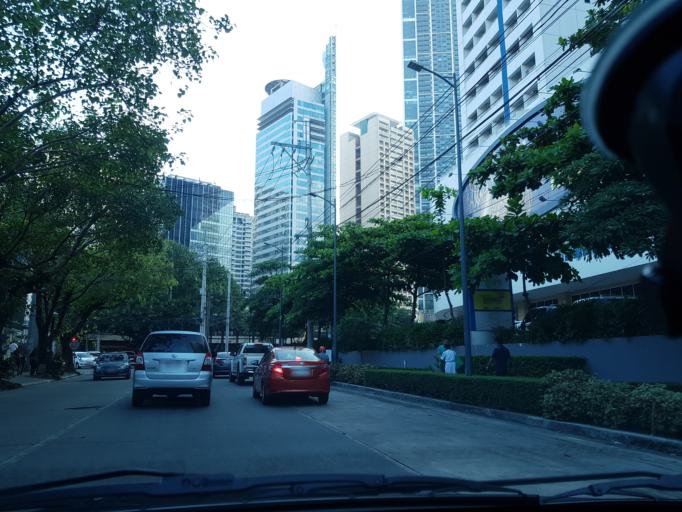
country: PH
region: Metro Manila
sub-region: Makati City
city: Makati City
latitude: 14.5636
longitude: 121.0223
